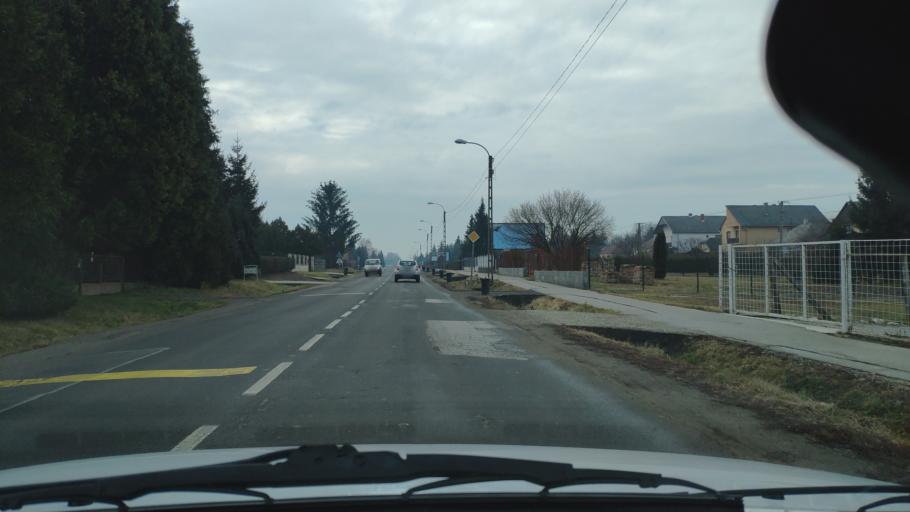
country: HU
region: Zala
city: Nagykanizsa
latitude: 46.4882
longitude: 16.9849
